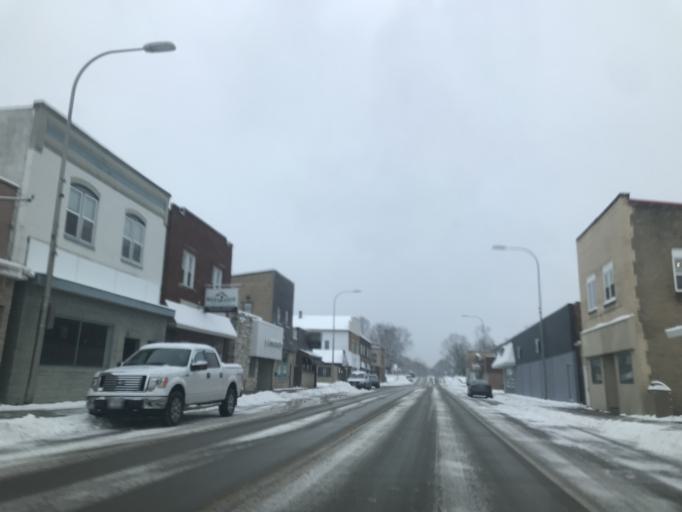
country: US
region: Wisconsin
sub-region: Oconto County
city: Oconto Falls
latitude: 44.8750
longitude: -88.1436
